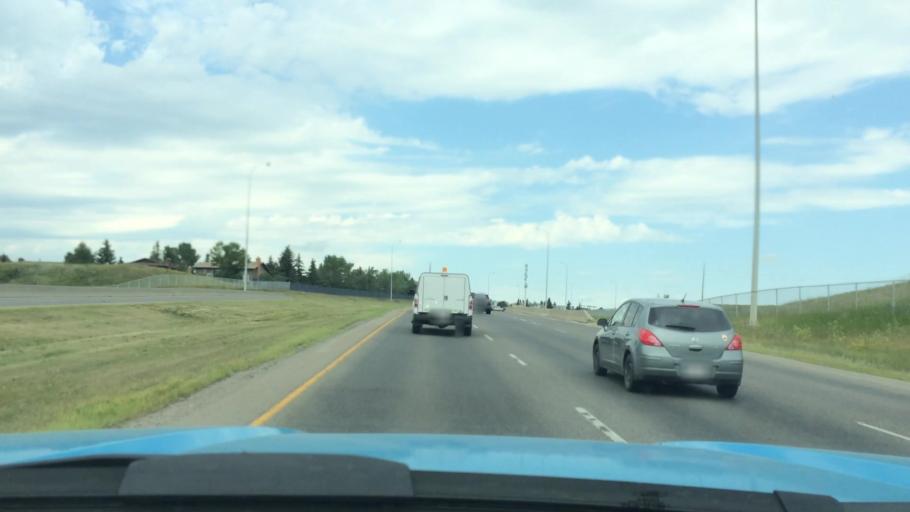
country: CA
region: Alberta
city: Calgary
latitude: 51.1215
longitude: -114.1343
